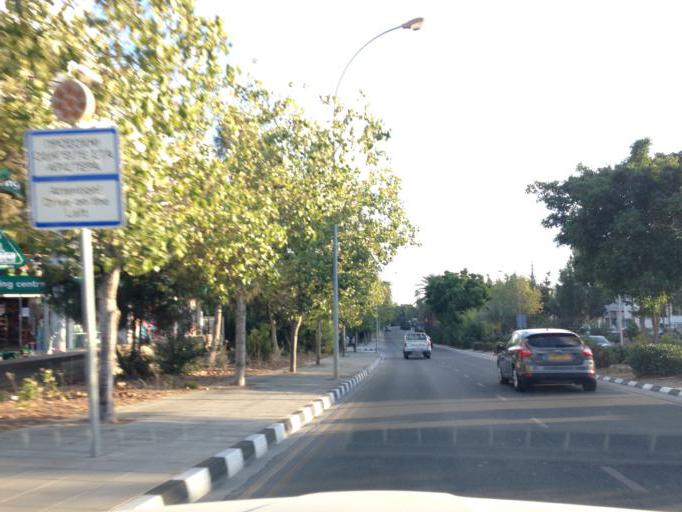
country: CY
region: Pafos
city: Paphos
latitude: 34.7666
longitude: 32.4403
